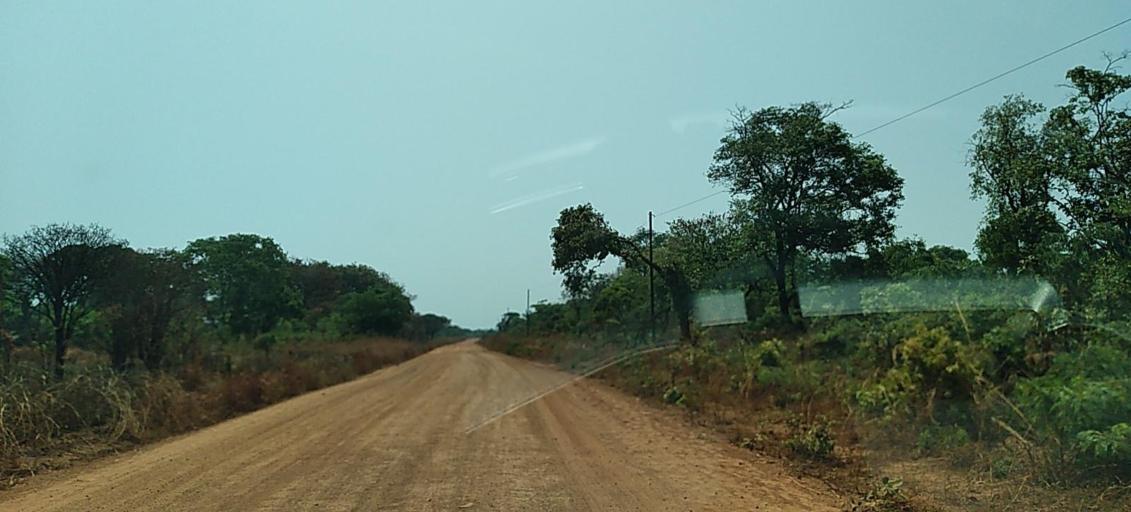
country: ZM
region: North-Western
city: Kansanshi
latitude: -11.9925
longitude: 26.6185
